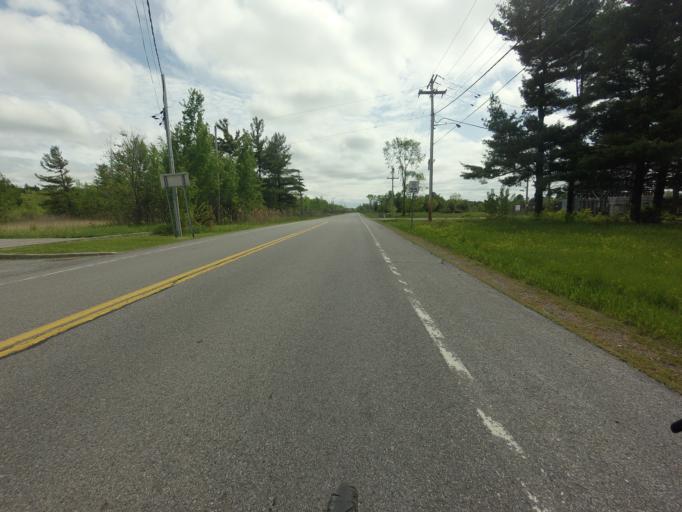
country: CA
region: Ontario
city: Cornwall
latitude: 44.9716
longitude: -74.6634
